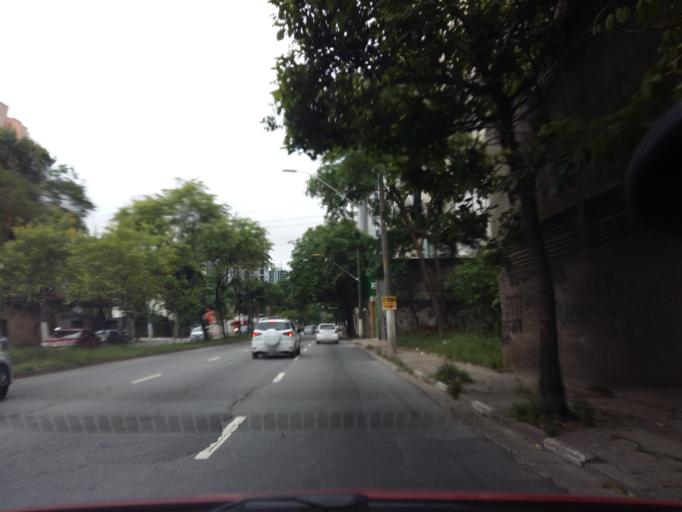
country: BR
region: Sao Paulo
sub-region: Santo Andre
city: Santo Andre
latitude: -23.6579
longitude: -46.5378
